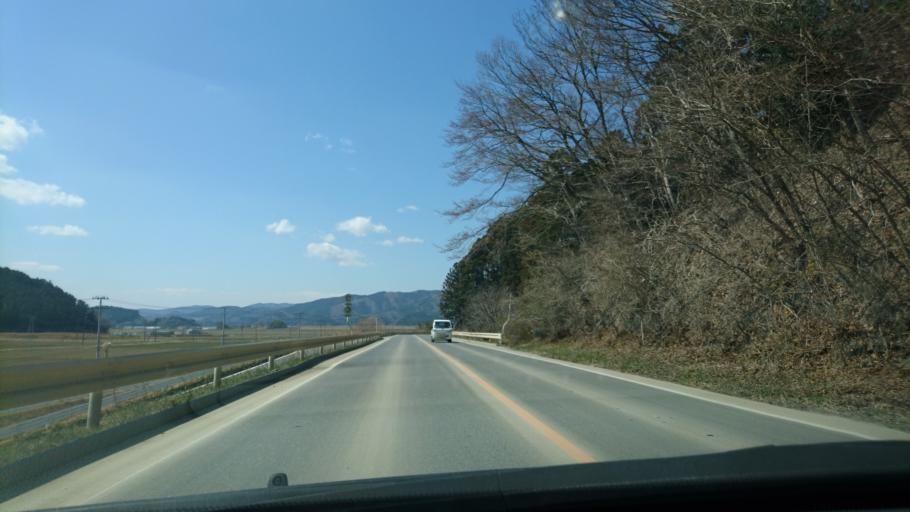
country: JP
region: Miyagi
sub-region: Oshika Gun
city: Onagawa Cho
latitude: 38.5360
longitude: 141.4324
